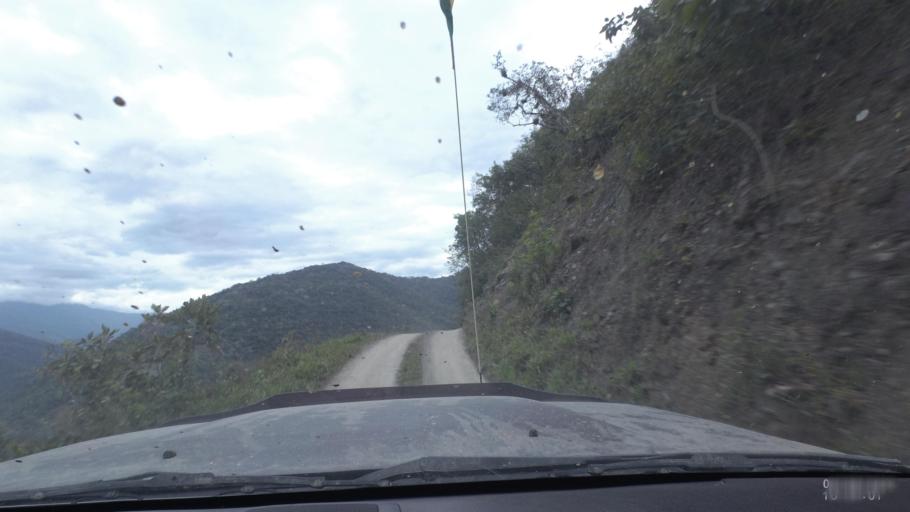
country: BO
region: La Paz
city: Quime
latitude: -16.5364
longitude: -66.7602
